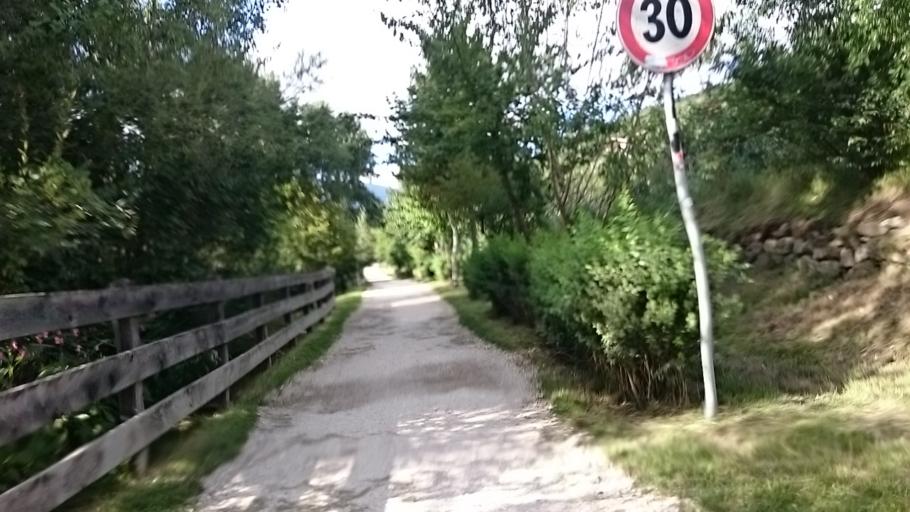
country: IT
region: Trentino-Alto Adige
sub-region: Bolzano
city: Leone-Santa Elisabetta
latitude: 46.7303
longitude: 11.6540
